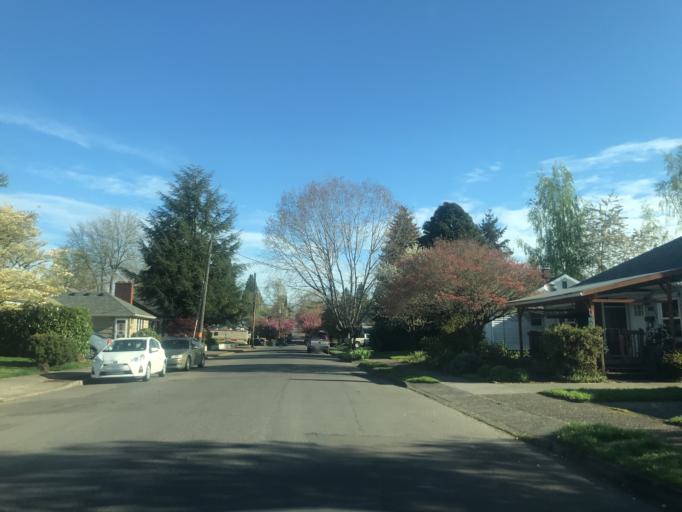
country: US
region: Oregon
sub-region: Multnomah County
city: Lents
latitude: 45.5004
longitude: -122.5829
